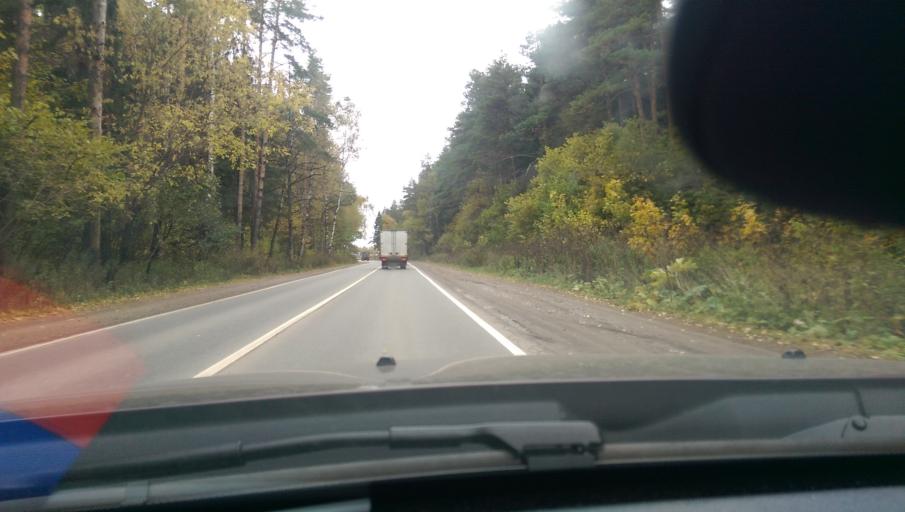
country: RU
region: Moskovskaya
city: Pirogovskiy
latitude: 55.9935
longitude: 37.7275
